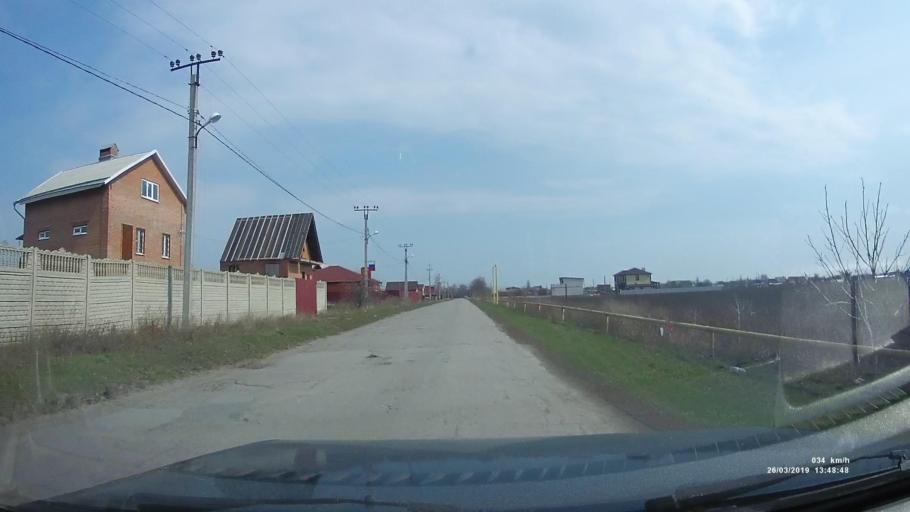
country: RU
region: Rostov
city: Novobessergenovka
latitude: 47.1918
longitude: 38.8610
